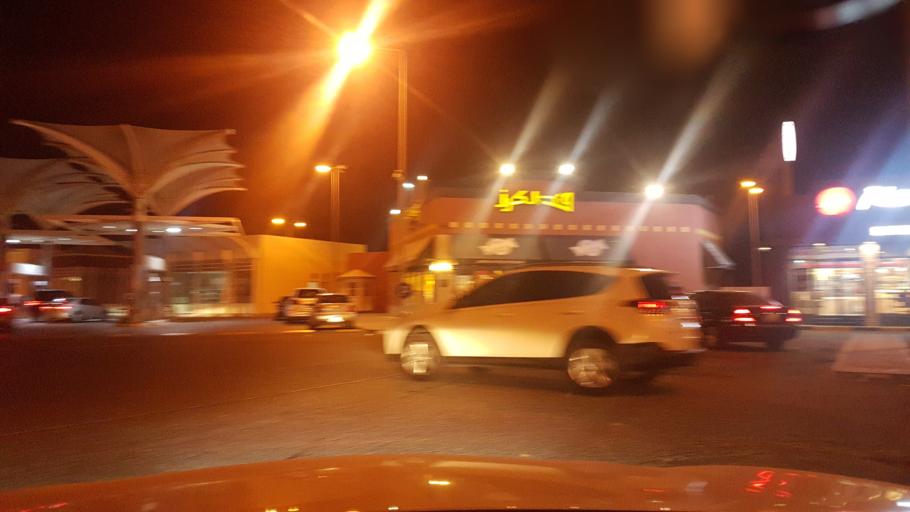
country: BH
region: Central Governorate
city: Dar Kulayb
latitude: 26.0503
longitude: 50.4992
